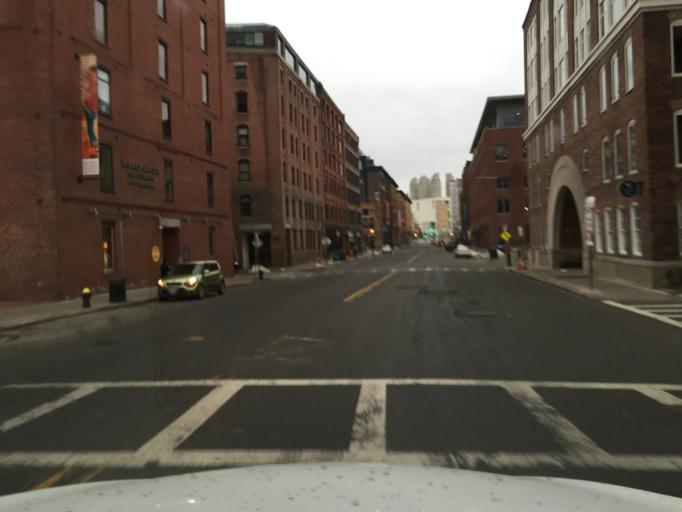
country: US
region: Massachusetts
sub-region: Suffolk County
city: Boston
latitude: 42.3516
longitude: -71.0504
